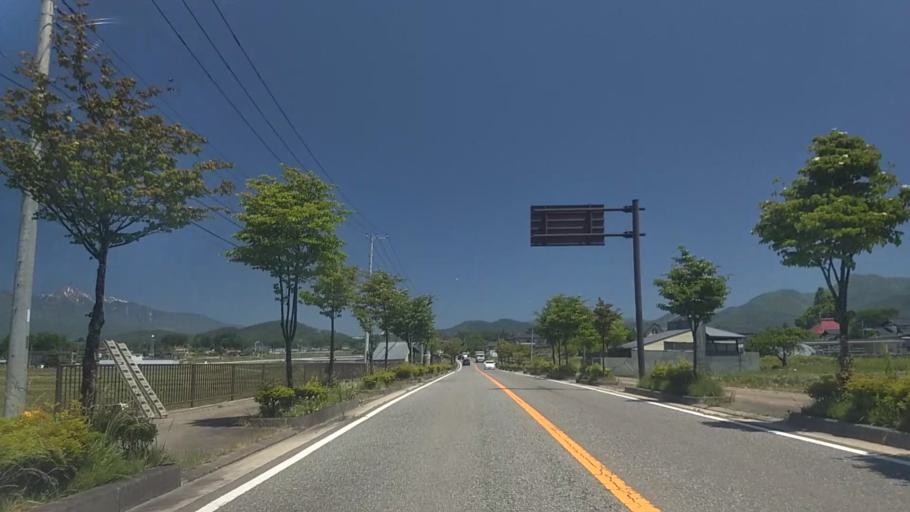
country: JP
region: Yamanashi
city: Nirasaki
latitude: 35.8263
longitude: 138.4291
